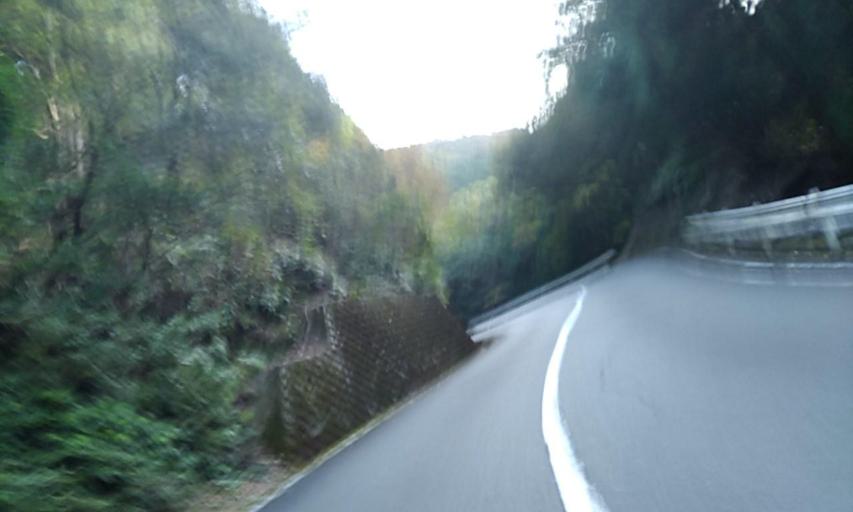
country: JP
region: Mie
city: Toba
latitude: 34.4785
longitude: 136.8325
